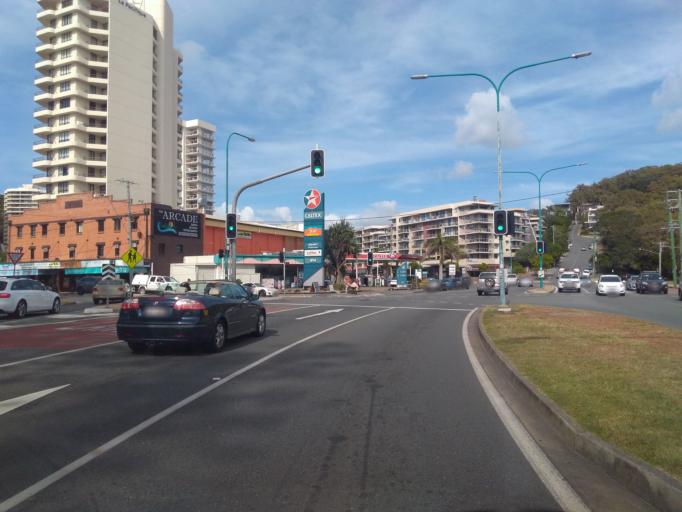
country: AU
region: Queensland
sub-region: Gold Coast
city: Burleigh Waters
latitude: -28.0893
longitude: 153.4529
